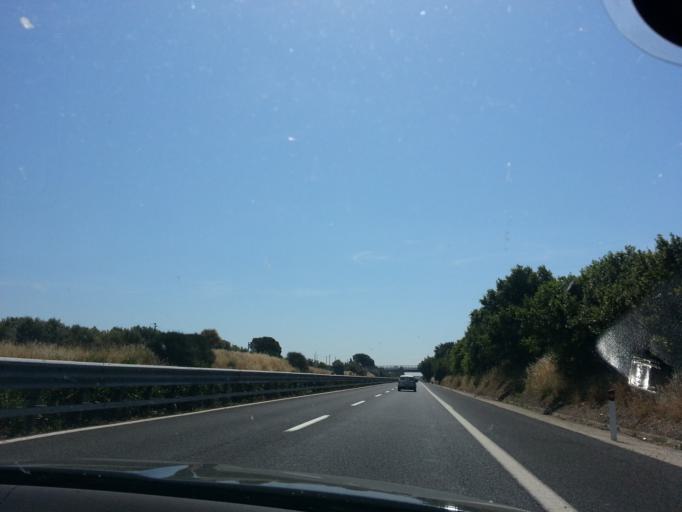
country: IT
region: Latium
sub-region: Citta metropolitana di Roma Capitale
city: Cerveteri
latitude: 41.9791
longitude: 12.0866
